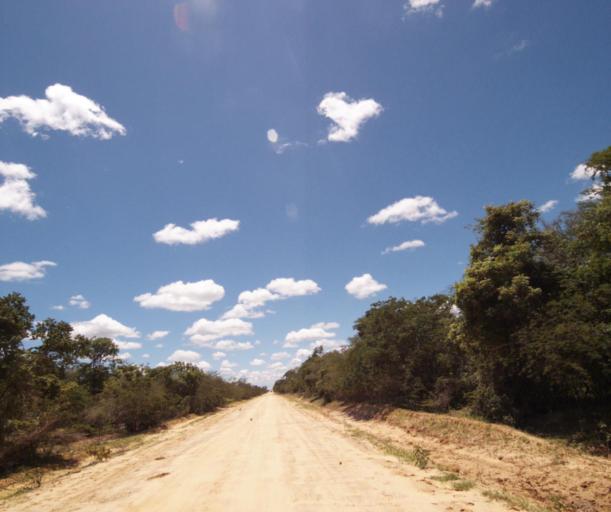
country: BR
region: Bahia
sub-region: Carinhanha
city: Carinhanha
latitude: -14.2100
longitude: -43.9426
